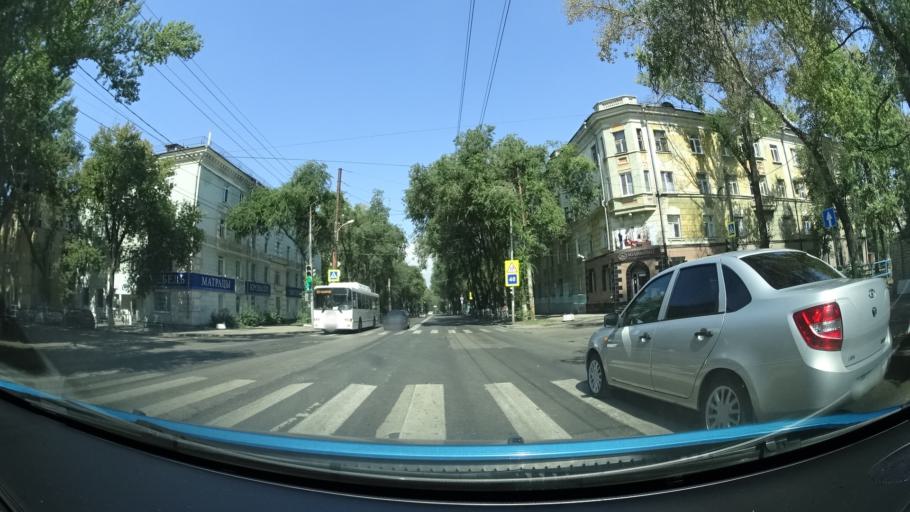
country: RU
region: Samara
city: Samara
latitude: 53.2070
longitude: 50.1610
